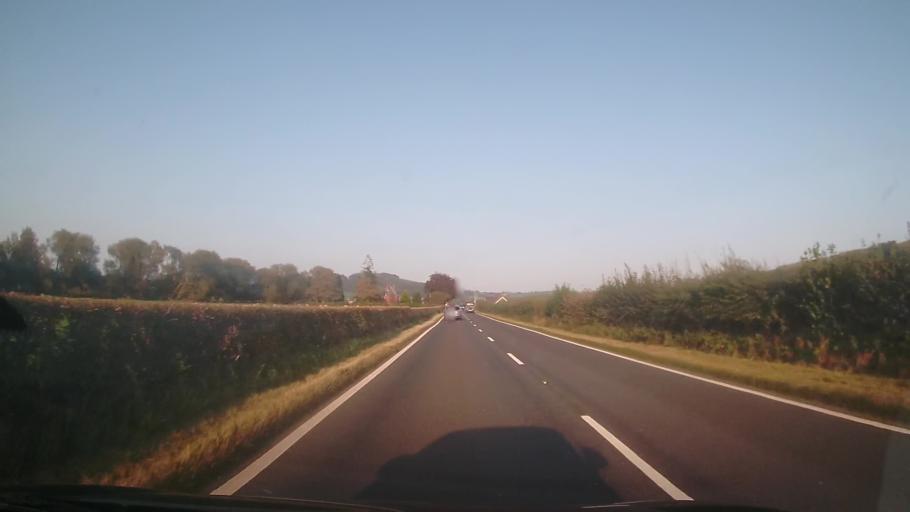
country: GB
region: Wales
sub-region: Sir Powys
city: Mochdre
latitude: 52.5149
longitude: -3.4093
